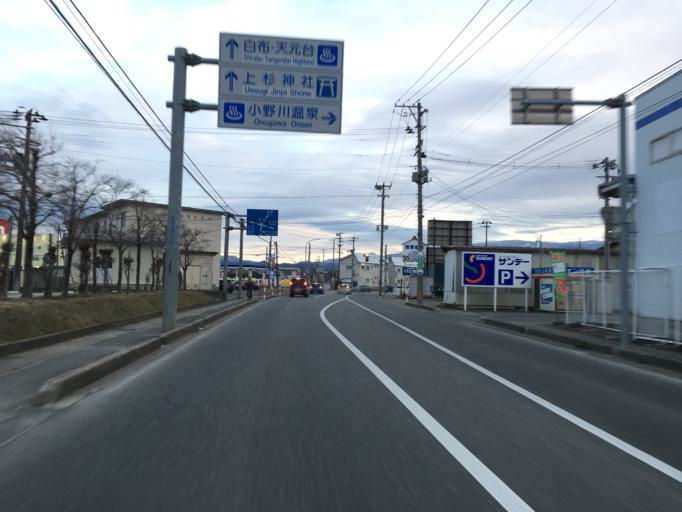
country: JP
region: Yamagata
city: Yonezawa
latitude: 37.9230
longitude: 140.0884
